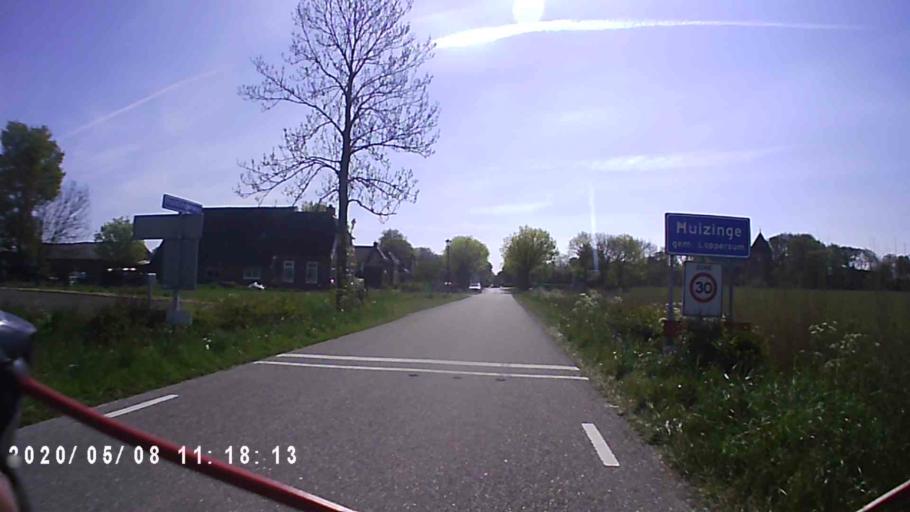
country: NL
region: Groningen
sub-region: Gemeente Bedum
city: Bedum
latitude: 53.3472
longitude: 6.6706
